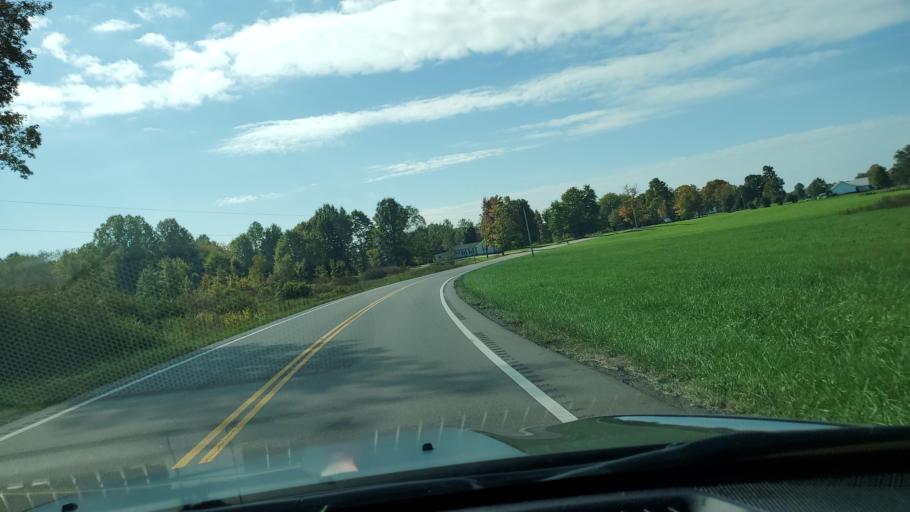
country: US
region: Ohio
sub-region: Trumbull County
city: Cortland
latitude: 41.4092
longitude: -80.6083
